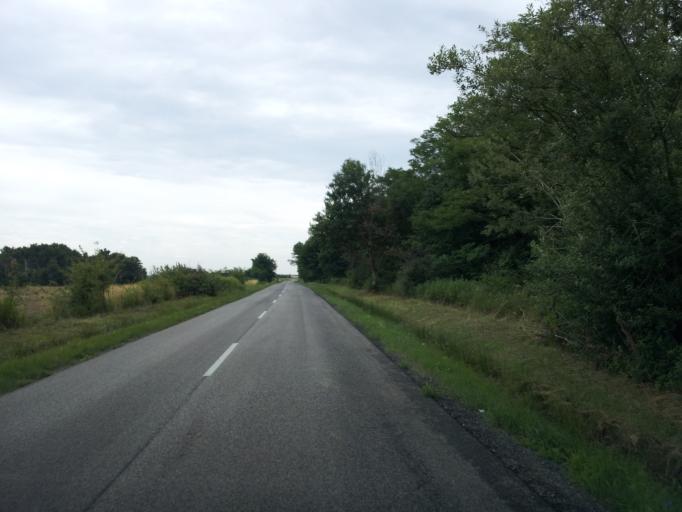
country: HU
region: Vas
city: Vasvar
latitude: 46.9696
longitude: 16.7153
